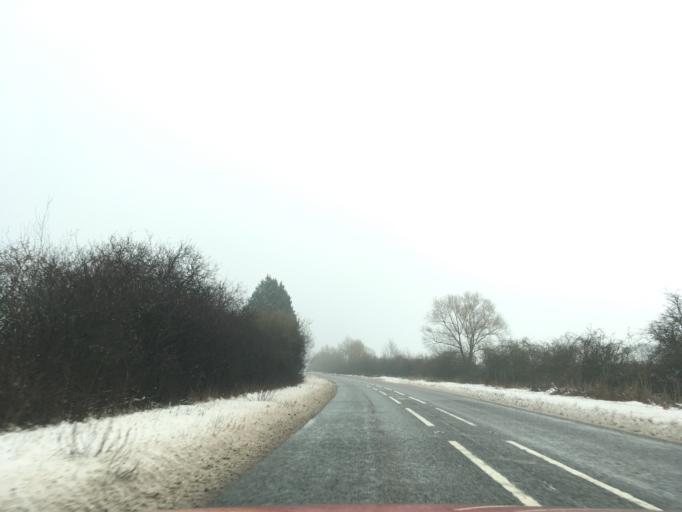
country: GB
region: England
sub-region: Worcestershire
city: Evesham
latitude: 52.0336
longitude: -1.9936
